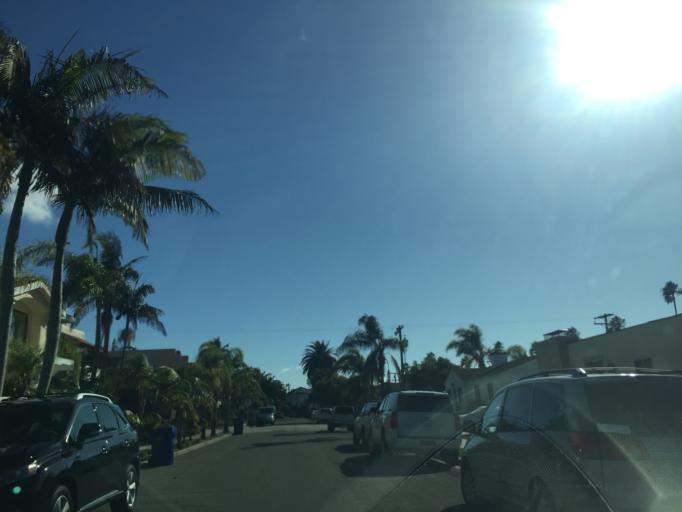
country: US
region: California
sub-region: San Diego County
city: La Jolla
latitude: 32.7830
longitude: -117.2385
